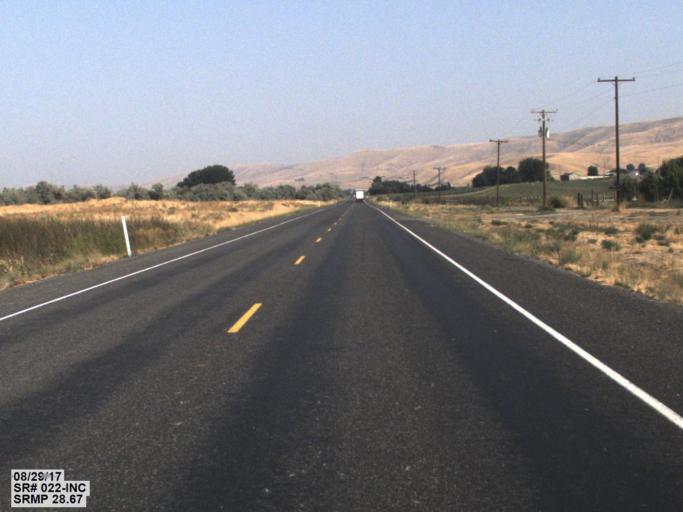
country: US
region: Washington
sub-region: Yakima County
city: Grandview
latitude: 46.1889
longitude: -119.8891
